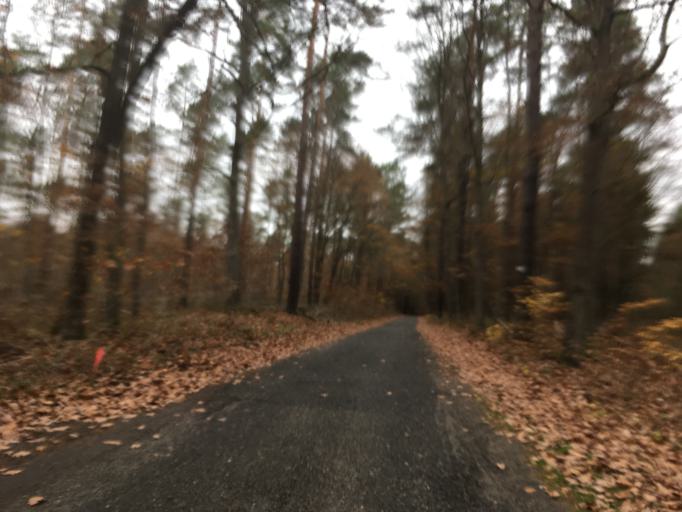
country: DE
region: Brandenburg
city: Mixdorf
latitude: 52.1738
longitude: 14.4379
